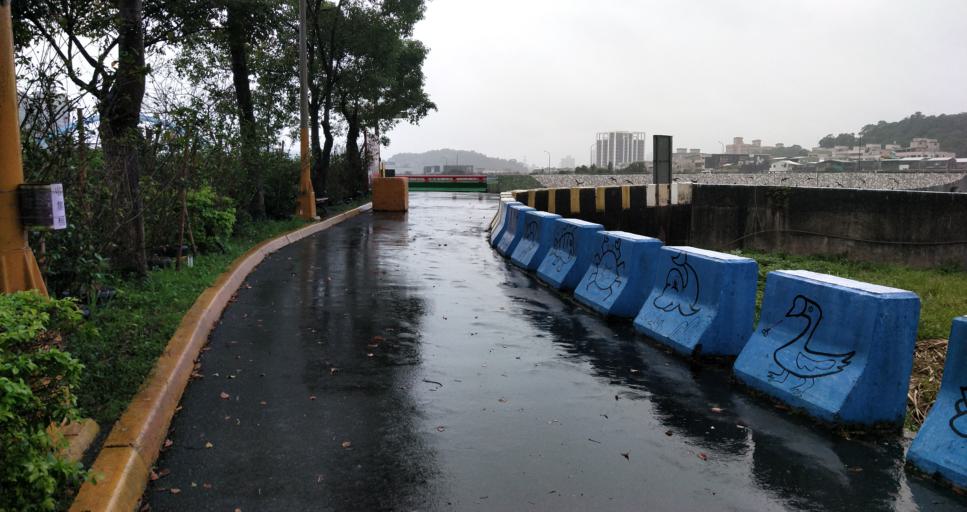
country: TW
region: Taiwan
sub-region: Keelung
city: Keelung
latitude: 25.0702
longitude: 121.6596
